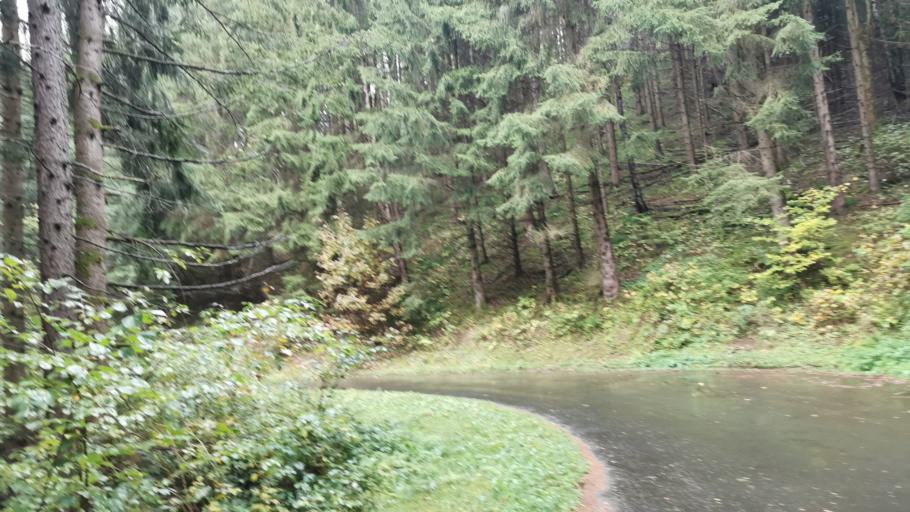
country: DE
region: Bavaria
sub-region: Upper Franconia
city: Nordhalben
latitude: 50.3409
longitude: 11.4920
